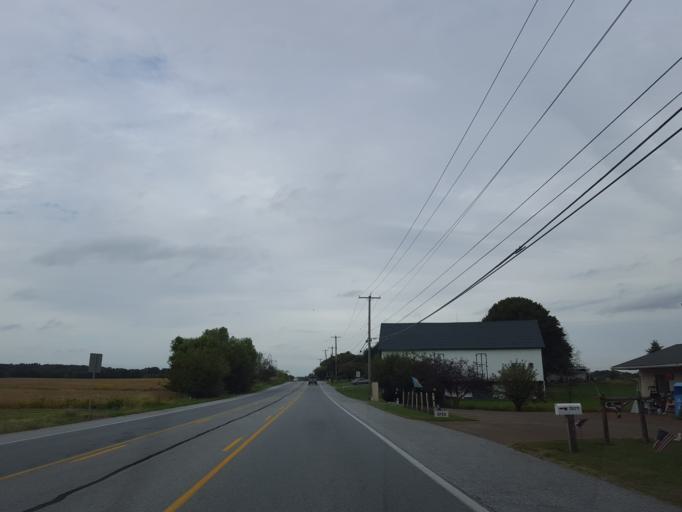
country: US
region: Pennsylvania
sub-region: Adams County
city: East Berlin
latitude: 39.9126
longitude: -76.9267
